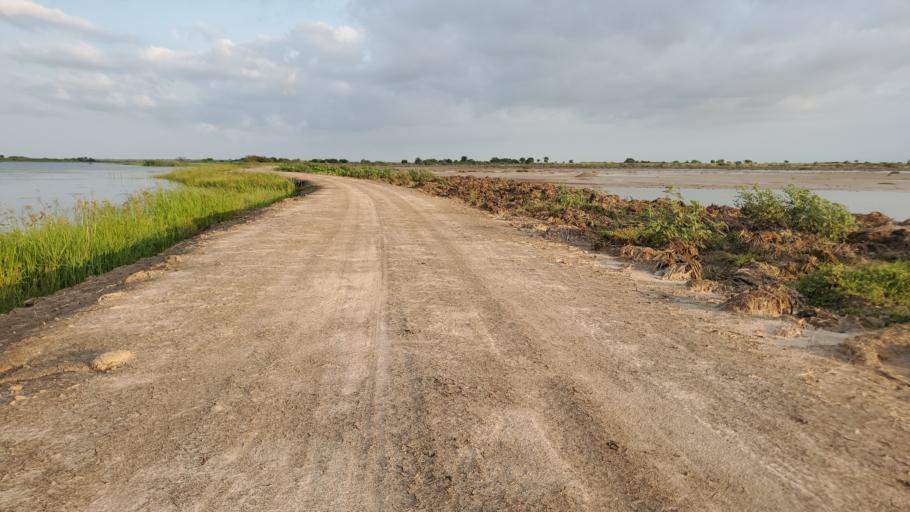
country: SN
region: Saint-Louis
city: Saint-Louis
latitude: 16.0201
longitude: -16.4067
